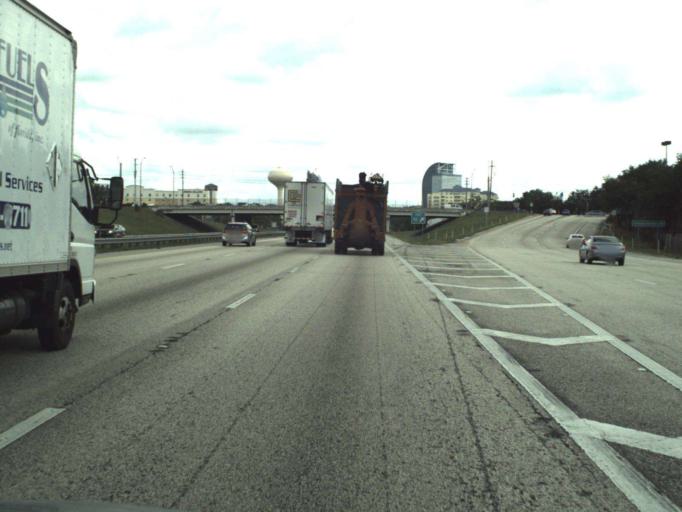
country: US
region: Florida
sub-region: Seminole County
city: Altamonte Springs
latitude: 28.6594
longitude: -81.3884
